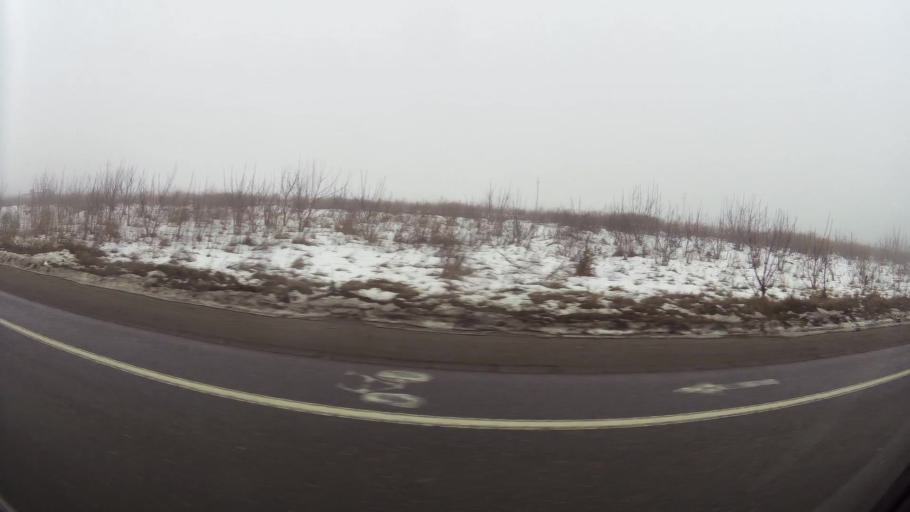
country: RO
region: Ilfov
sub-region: Comuna Chiajna
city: Chiajna
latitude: 44.4524
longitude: 25.9679
